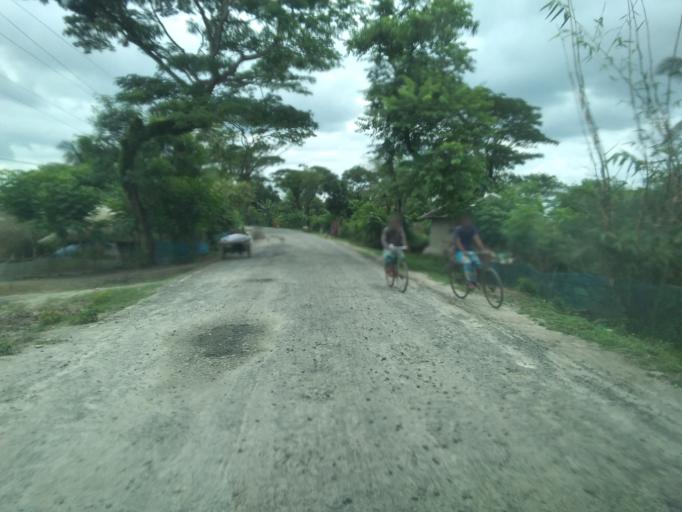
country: IN
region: West Bengal
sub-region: North 24 Parganas
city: Gosaba
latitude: 22.2667
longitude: 89.1661
